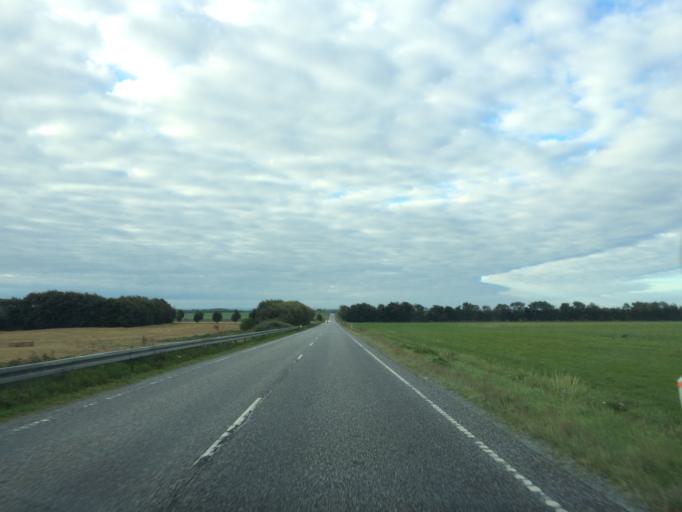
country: DK
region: Central Jutland
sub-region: Ringkobing-Skjern Kommune
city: Skjern
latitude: 56.0128
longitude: 8.5029
